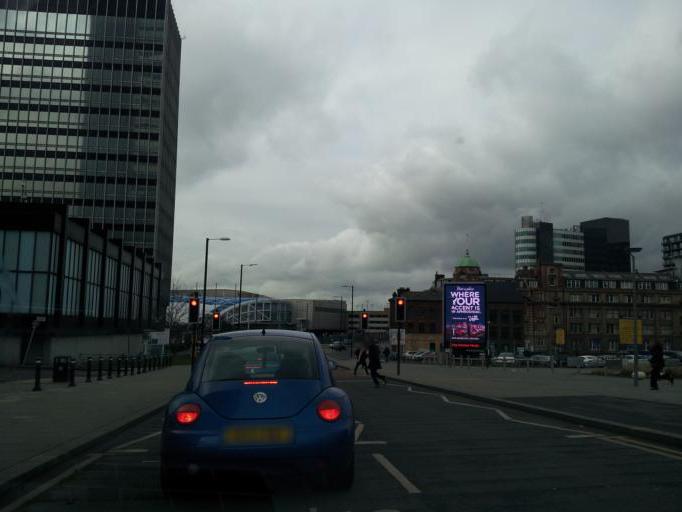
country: GB
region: England
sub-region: Manchester
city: Manchester
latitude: 53.4870
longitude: -2.2381
